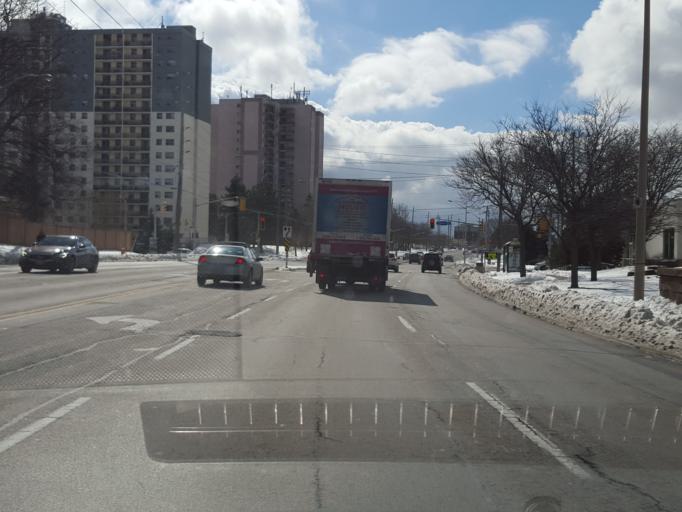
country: CA
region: Ontario
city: Burlington
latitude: 43.3253
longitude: -79.8284
